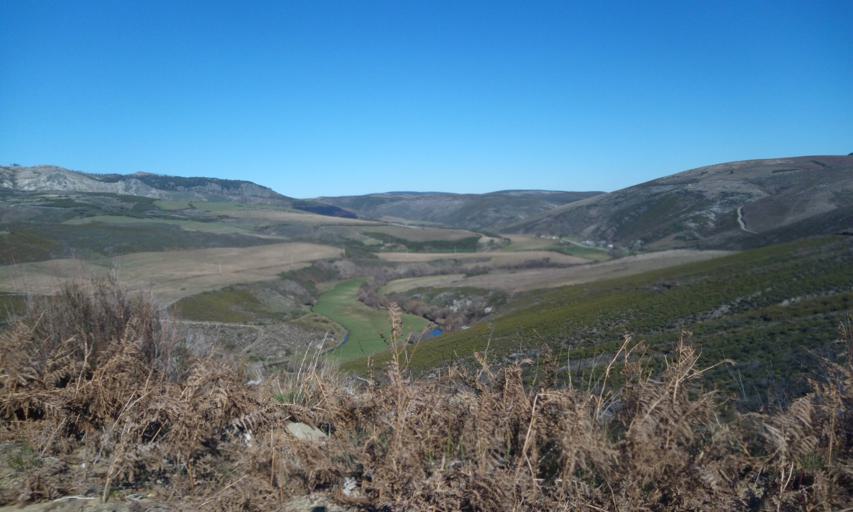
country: PT
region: Guarda
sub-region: Manteigas
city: Manteigas
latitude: 40.4483
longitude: -7.5053
